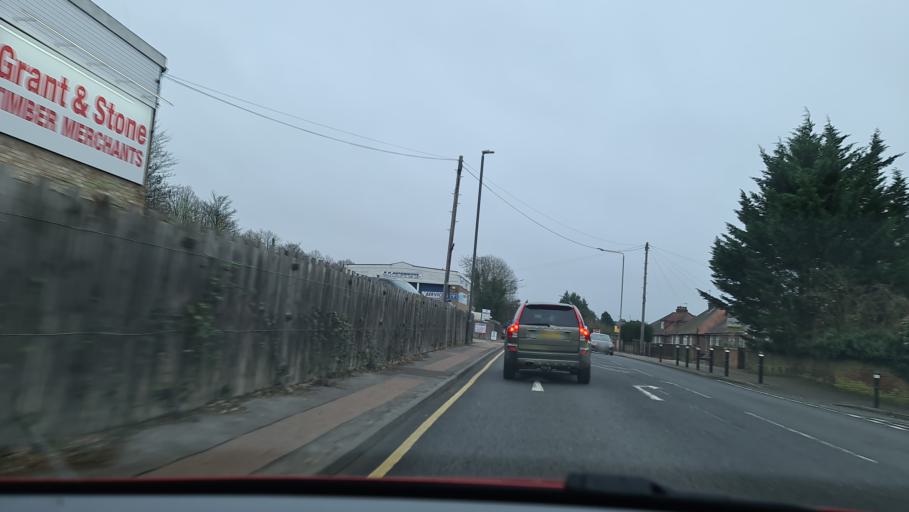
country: GB
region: England
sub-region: Buckinghamshire
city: High Wycombe
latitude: 51.6421
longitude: -0.7879
